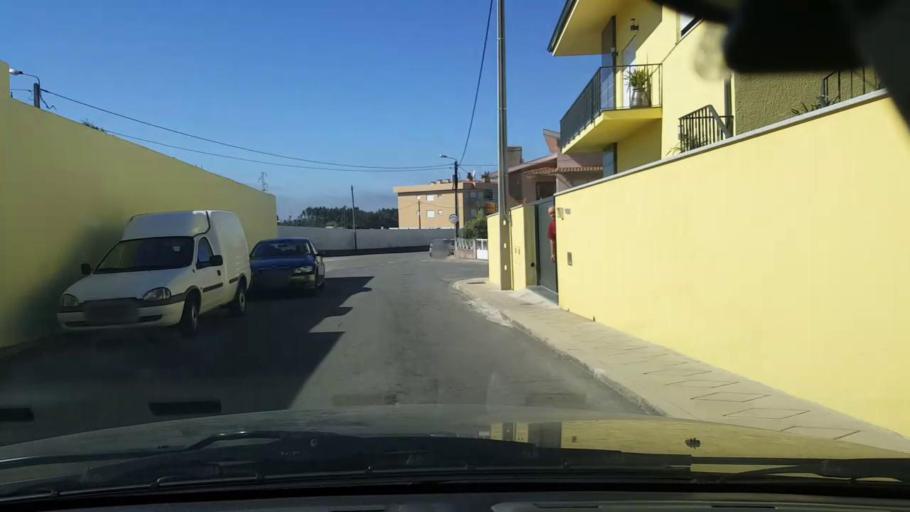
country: PT
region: Porto
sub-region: Maia
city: Gemunde
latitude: 41.2883
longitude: -8.6415
